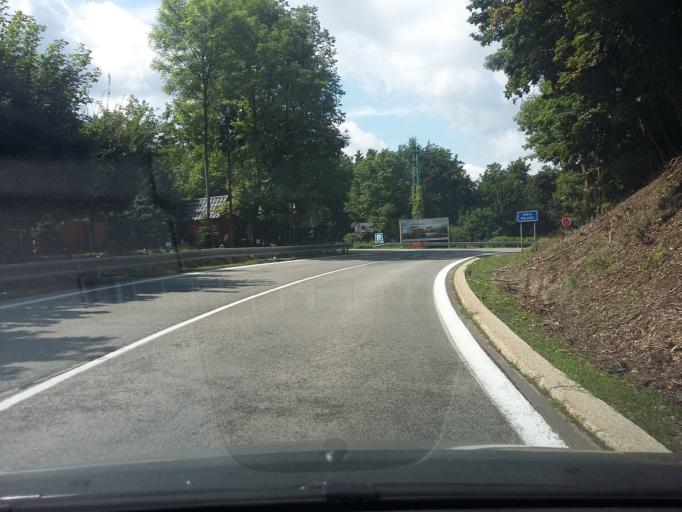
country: SK
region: Bratislavsky
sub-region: Okres Pezinok
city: Pezinok
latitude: 48.3507
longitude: 17.1899
